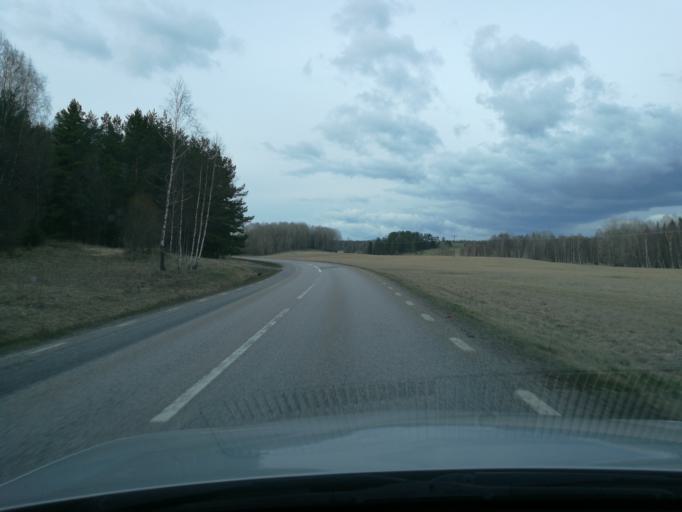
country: SE
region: Soedermanland
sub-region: Gnesta Kommun
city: Gnesta
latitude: 58.9349
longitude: 17.3467
